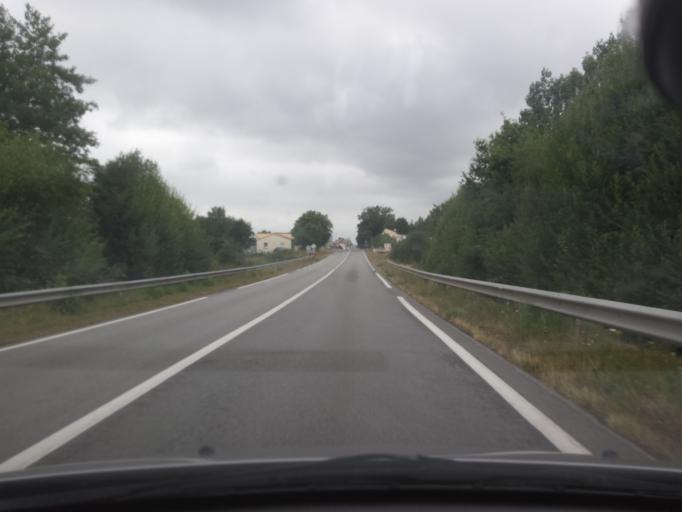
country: FR
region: Pays de la Loire
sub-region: Departement de la Vendee
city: Chateau-Guibert
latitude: 46.5691
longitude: -1.2779
